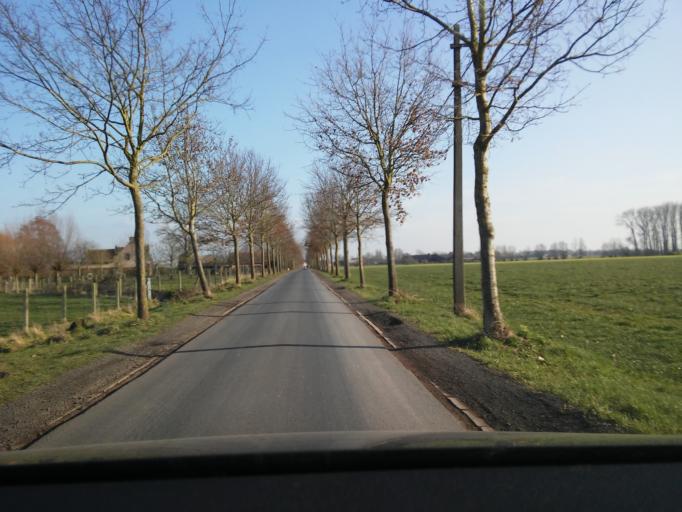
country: BE
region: Flanders
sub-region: Provincie Oost-Vlaanderen
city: Aalter
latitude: 51.0406
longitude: 3.4572
